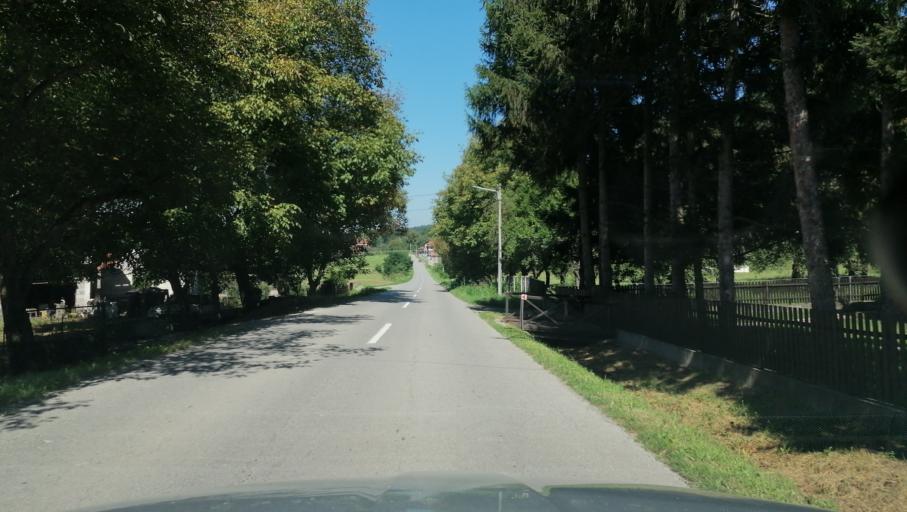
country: RS
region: Central Serbia
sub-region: Raski Okrug
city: Vrnjacka Banja
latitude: 43.6758
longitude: 20.8995
